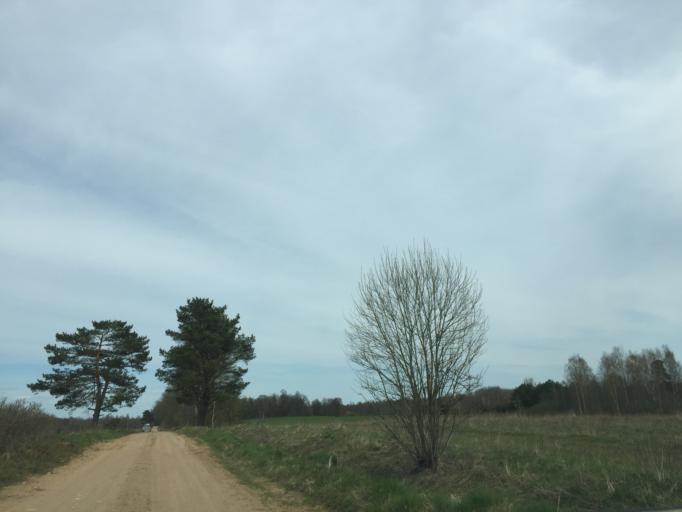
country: LV
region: Ludzas Rajons
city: Ludza
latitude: 56.5164
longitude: 27.5704
